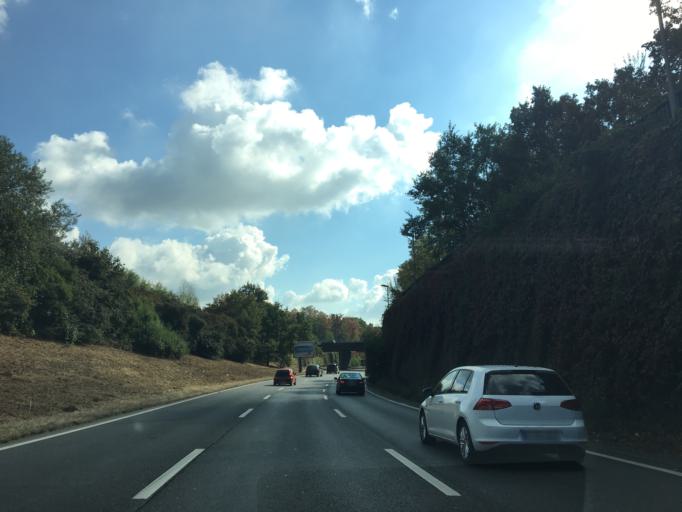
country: DE
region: North Rhine-Westphalia
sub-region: Regierungsbezirk Dusseldorf
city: Dusseldorf
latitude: 51.1983
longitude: 6.7741
